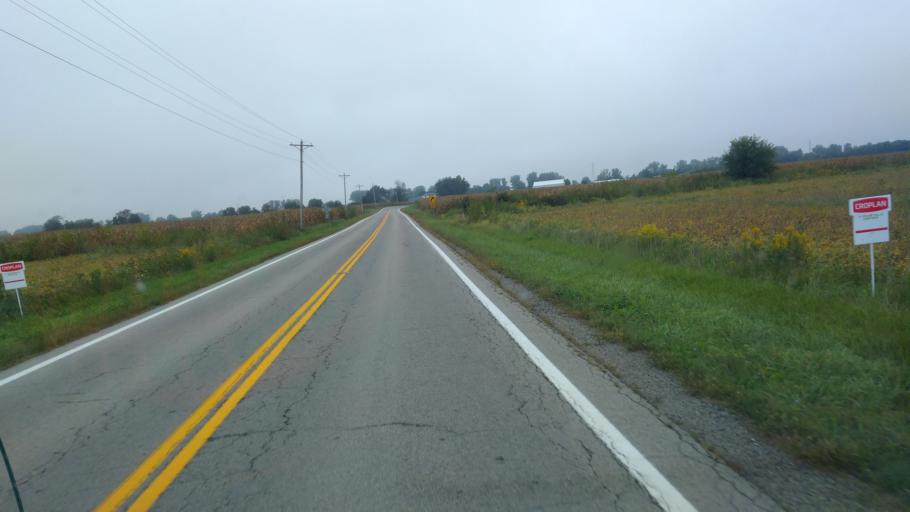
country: US
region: Ohio
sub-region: Logan County
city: Northwood
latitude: 40.4756
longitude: -83.5784
